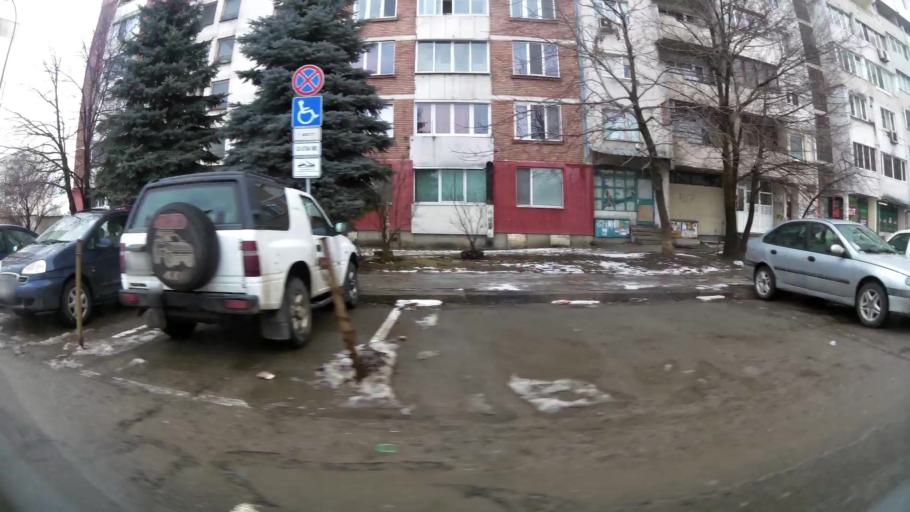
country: BG
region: Sofiya
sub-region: Obshtina Bozhurishte
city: Bozhurishte
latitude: 42.7174
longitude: 23.2378
